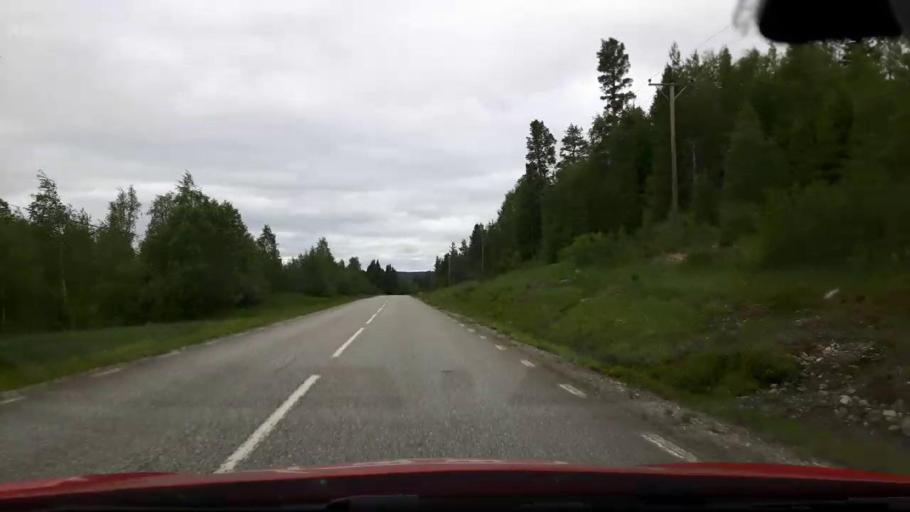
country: SE
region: Jaemtland
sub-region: Stroemsunds Kommun
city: Stroemsund
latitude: 63.3157
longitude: 15.7627
